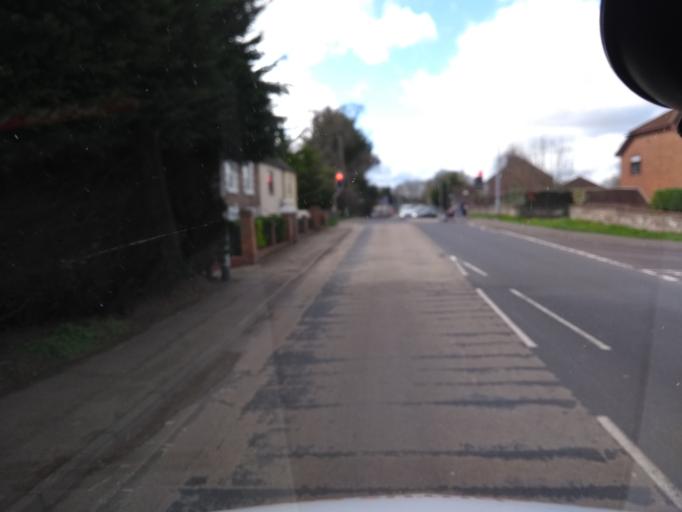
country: GB
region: England
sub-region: Somerset
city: Creech Saint Michael
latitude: 51.0277
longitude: -3.0665
